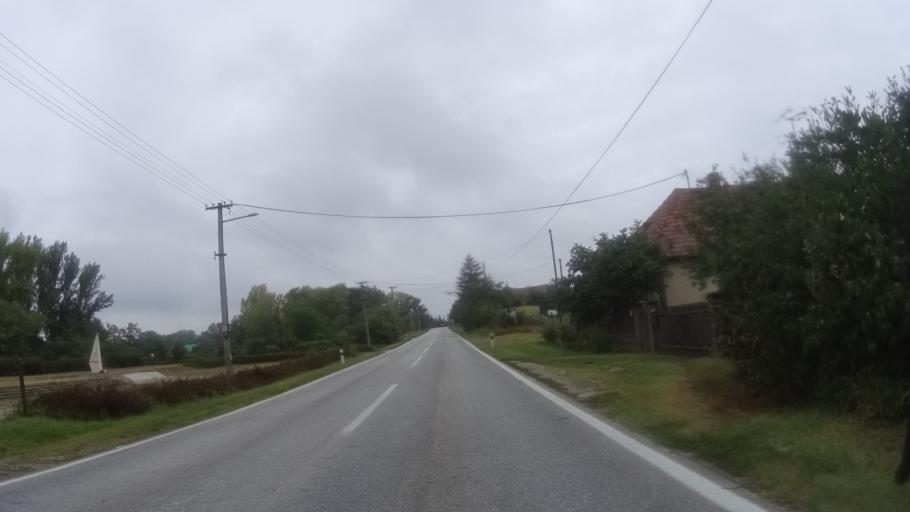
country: HU
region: Komarom-Esztergom
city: Neszmely
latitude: 47.7450
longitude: 18.3450
